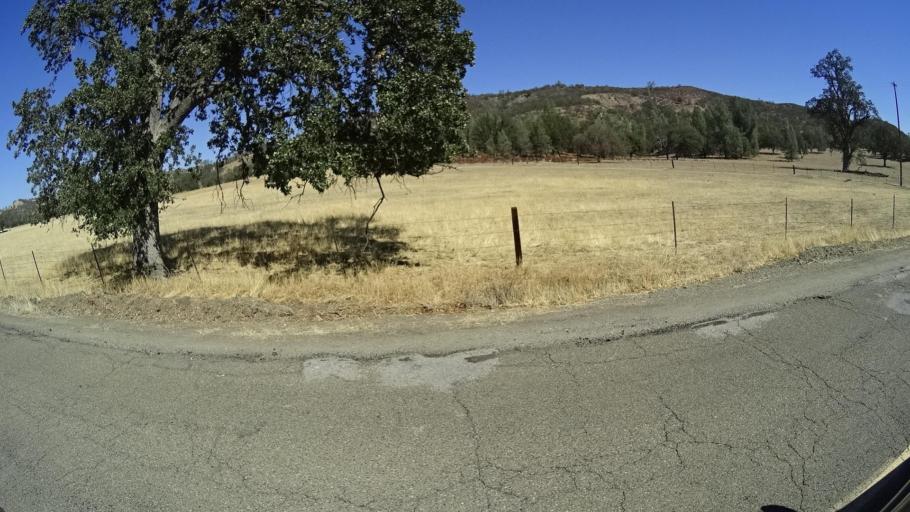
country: US
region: California
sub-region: Fresno County
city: Coalinga
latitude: 35.9217
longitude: -120.4948
